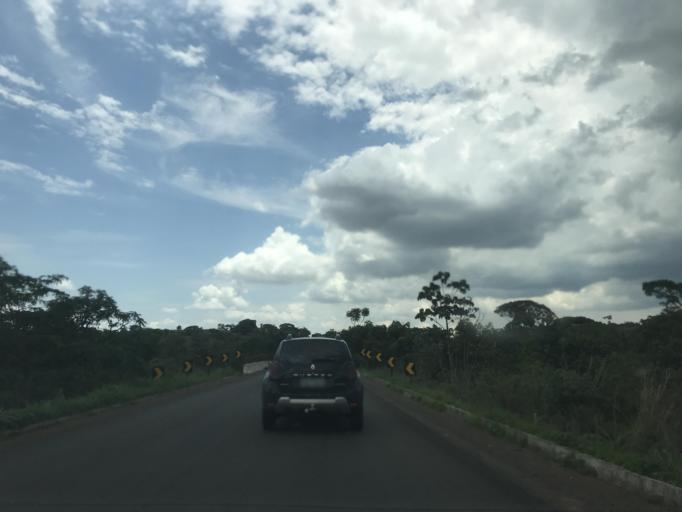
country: BR
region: Goias
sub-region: Vianopolis
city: Vianopolis
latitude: -16.9472
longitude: -48.5808
